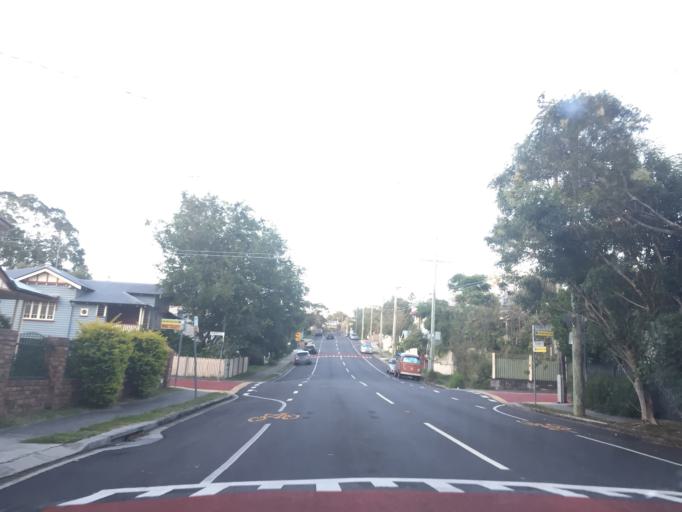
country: AU
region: Queensland
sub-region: Brisbane
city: Milton
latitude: -27.4626
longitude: 152.9967
